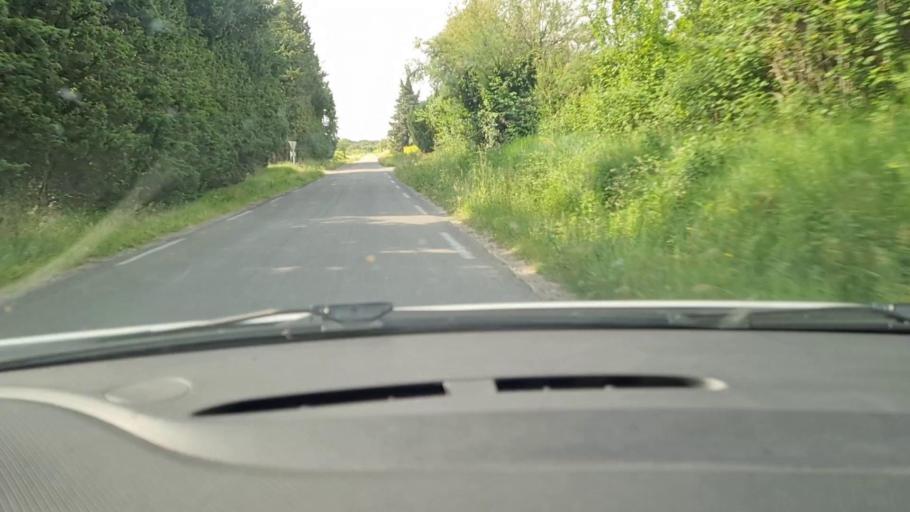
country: FR
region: Languedoc-Roussillon
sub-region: Departement du Gard
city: Jonquieres-Saint-Vincent
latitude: 43.8209
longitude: 4.5571
